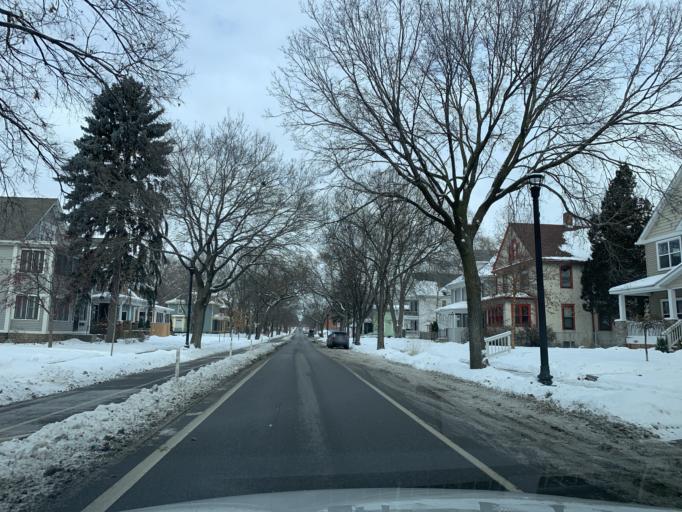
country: US
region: Minnesota
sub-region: Hennepin County
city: Minneapolis
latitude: 44.9954
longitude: -93.2941
